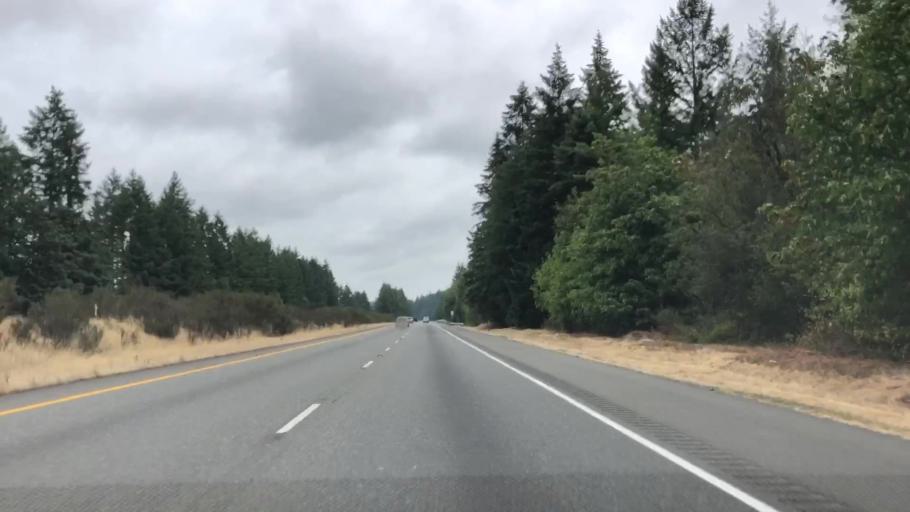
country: US
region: Washington
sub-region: Kitsap County
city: Burley
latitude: 47.4436
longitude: -122.6222
